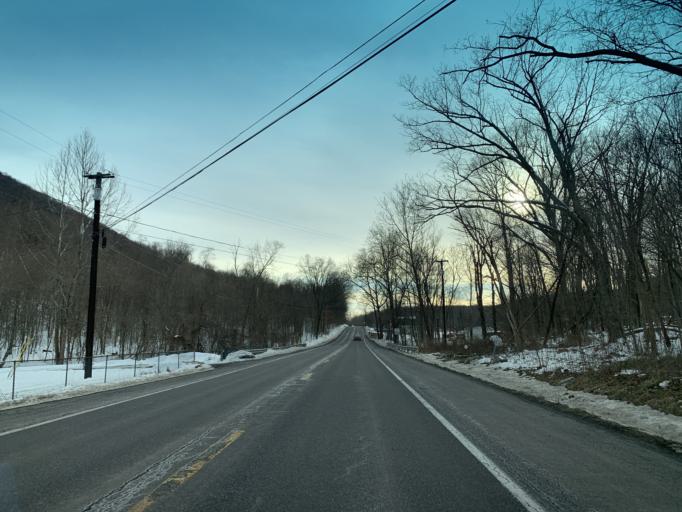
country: US
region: Maryland
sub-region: Allegany County
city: Bel Air
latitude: 39.5240
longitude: -78.9051
